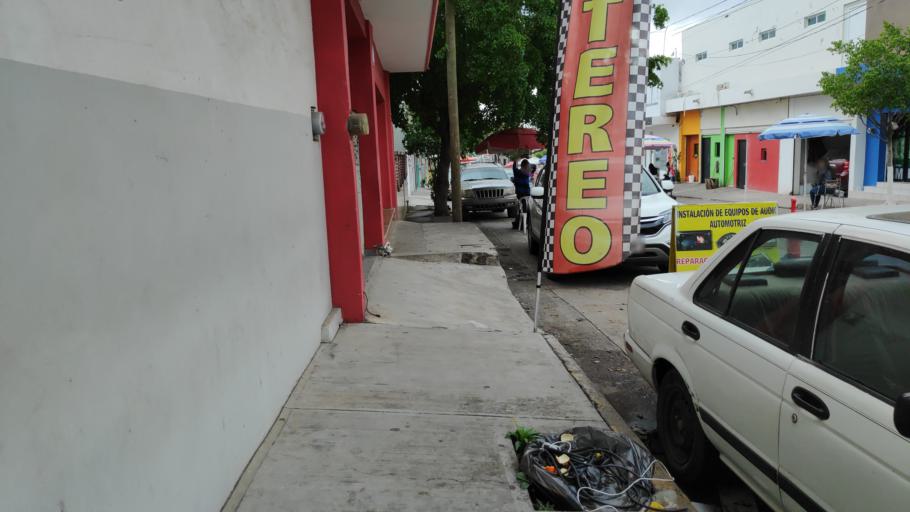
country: MX
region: Sinaloa
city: Culiacan
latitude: 24.8071
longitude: -107.3858
